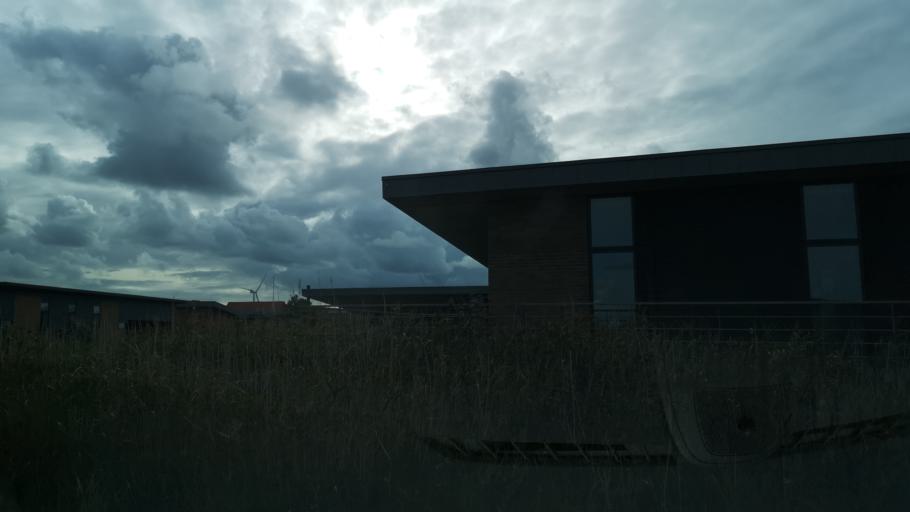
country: DK
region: Central Jutland
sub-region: Ringkobing-Skjern Kommune
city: Hvide Sande
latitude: 56.0098
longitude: 8.1330
